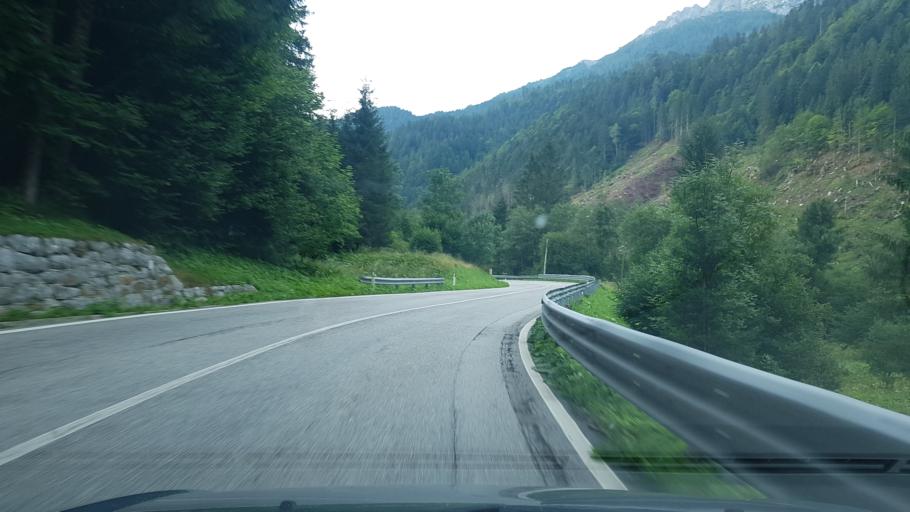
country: IT
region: Friuli Venezia Giulia
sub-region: Provincia di Udine
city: Forni Avoltri
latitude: 46.5790
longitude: 12.7903
